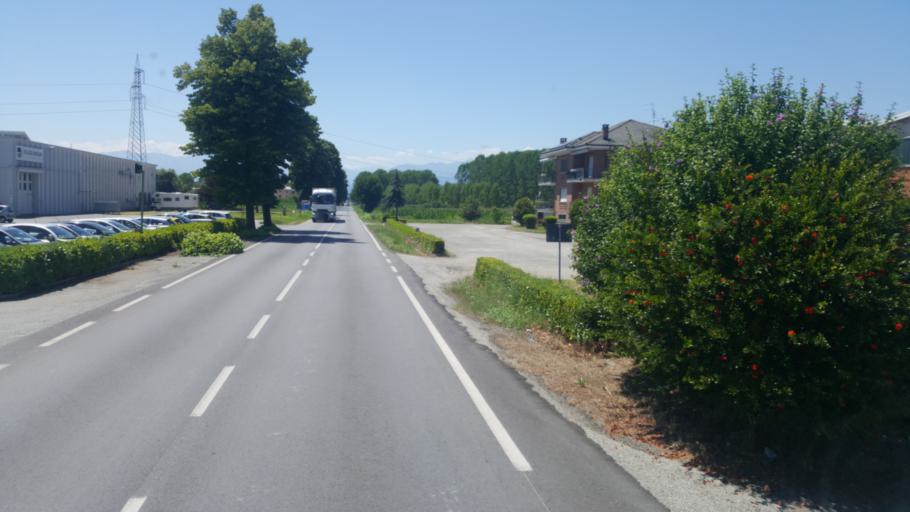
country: IT
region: Piedmont
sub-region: Provincia di Torino
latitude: 44.9276
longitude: 7.5220
